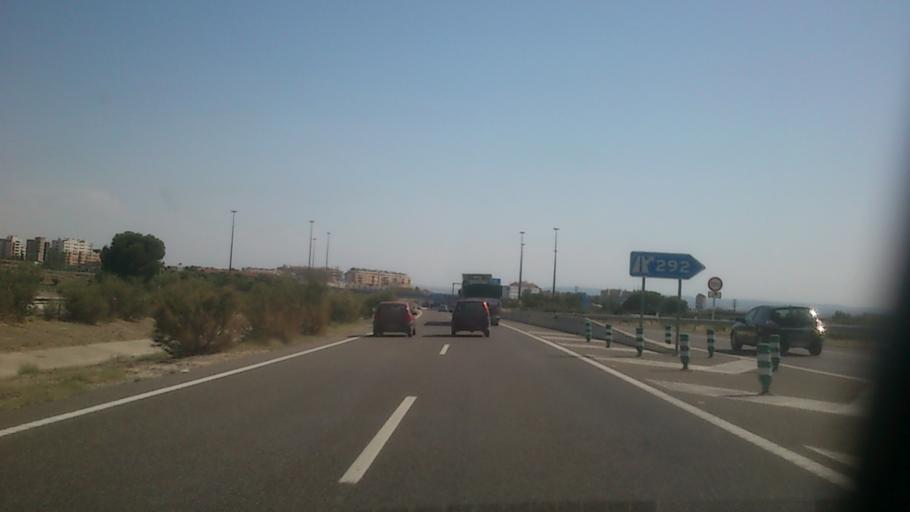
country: ES
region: Aragon
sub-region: Provincia de Zaragoza
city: Zaragoza
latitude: 41.6806
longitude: -0.8344
